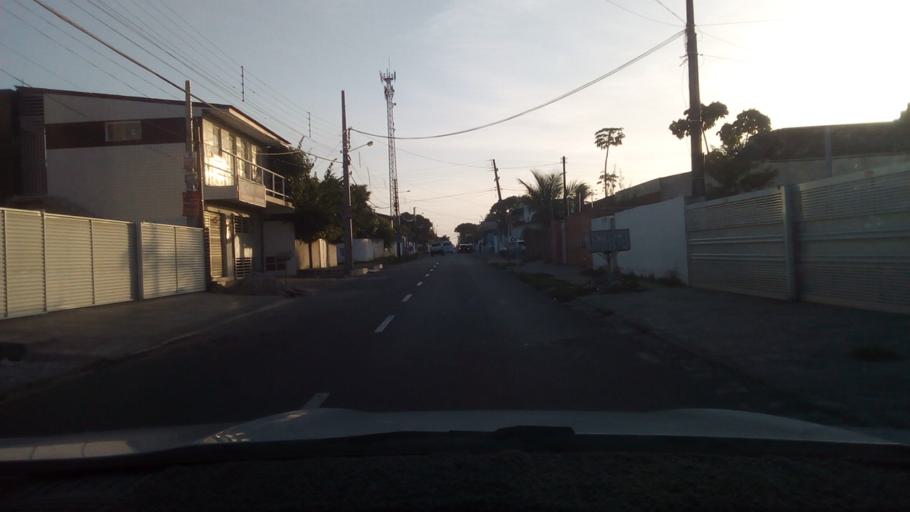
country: BR
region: Paraiba
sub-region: Bayeux
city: Bayeux
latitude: -7.1754
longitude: -34.9177
